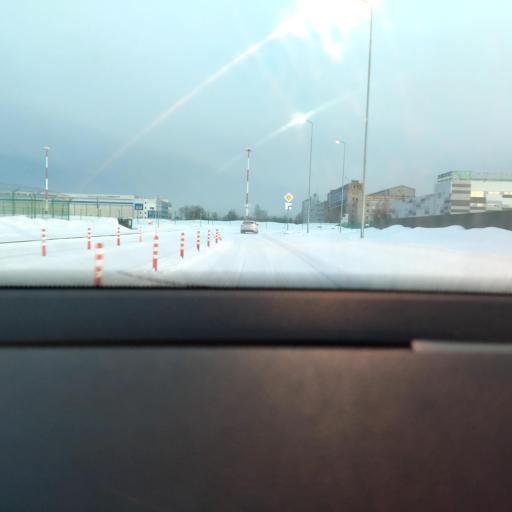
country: RU
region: Moskovskaya
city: Zhukovskiy
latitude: 55.5598
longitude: 38.1190
